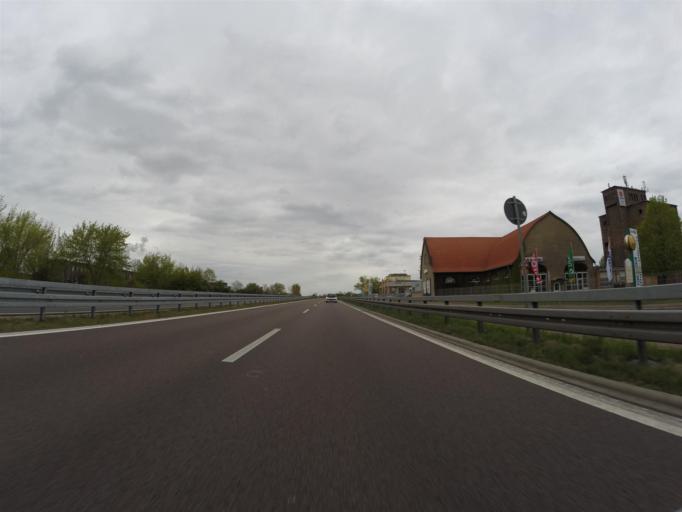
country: DE
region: Saxony-Anhalt
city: Schkopau
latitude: 51.3942
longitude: 11.9766
